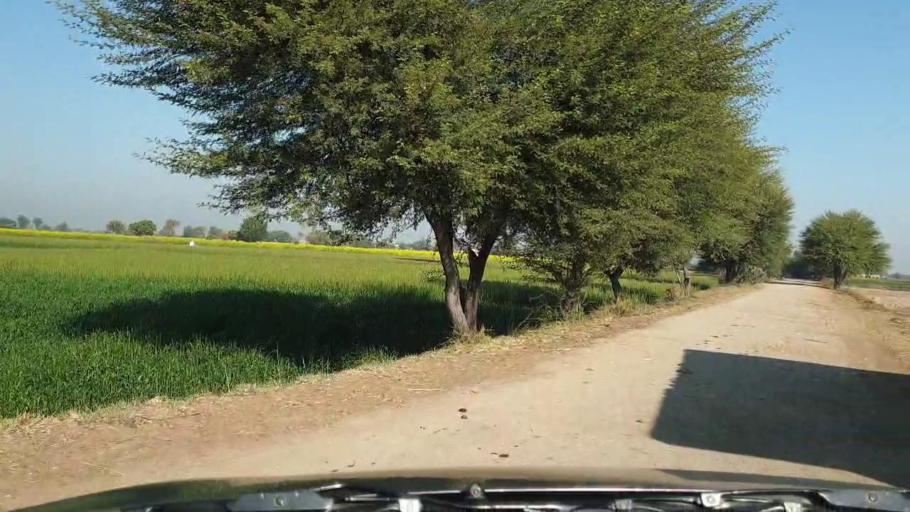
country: PK
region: Sindh
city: Jhol
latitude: 25.9431
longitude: 68.8219
